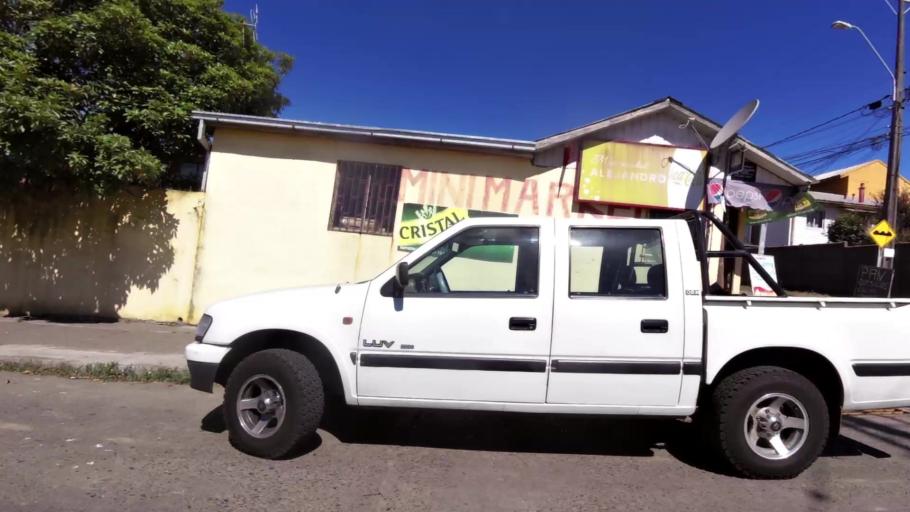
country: CL
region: Biobio
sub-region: Provincia de Concepcion
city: Penco
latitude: -36.7243
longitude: -72.9845
